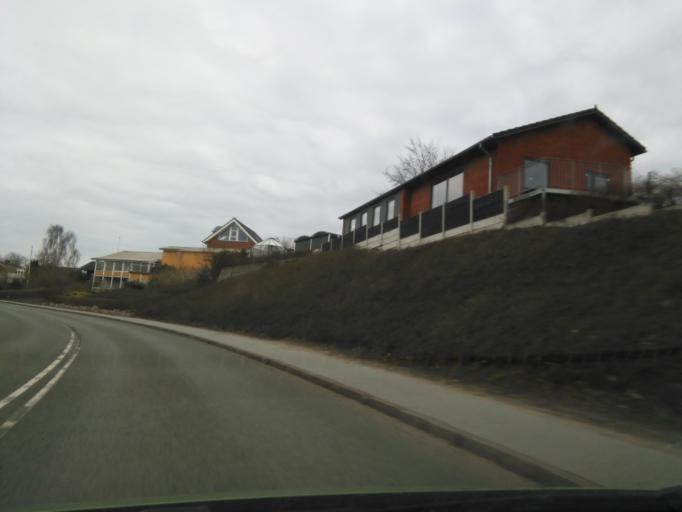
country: DK
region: North Denmark
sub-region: Mariagerfjord Kommune
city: Mariager
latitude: 56.6526
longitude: 9.9763
